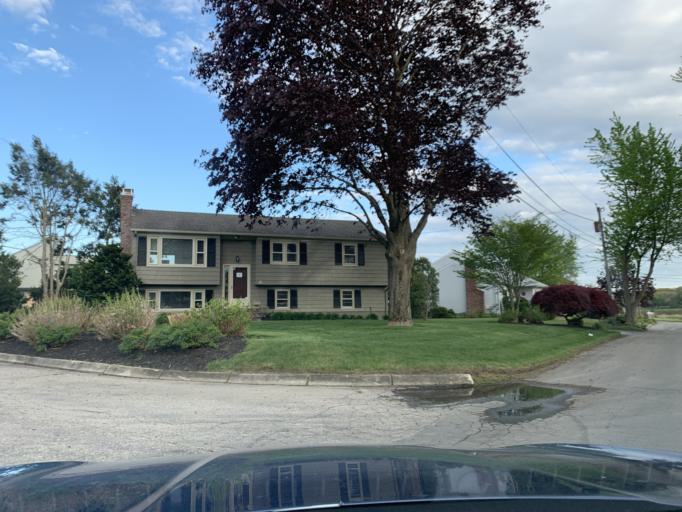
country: US
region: Rhode Island
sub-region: Kent County
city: East Greenwich
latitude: 41.6599
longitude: -71.4160
